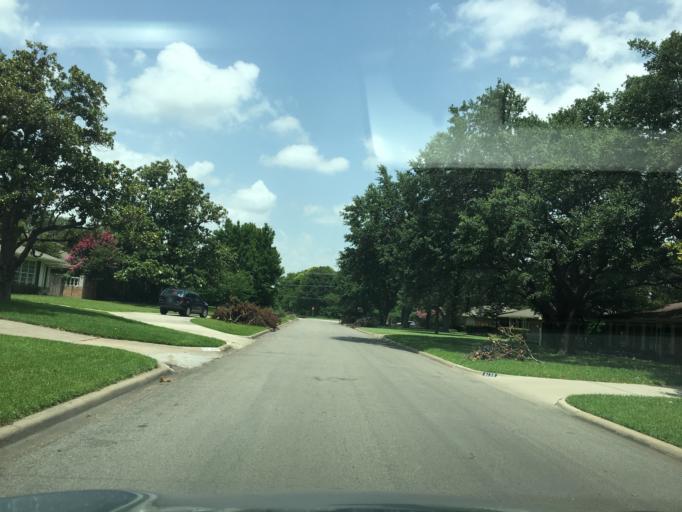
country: US
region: Texas
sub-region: Dallas County
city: University Park
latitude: 32.9082
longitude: -96.8009
